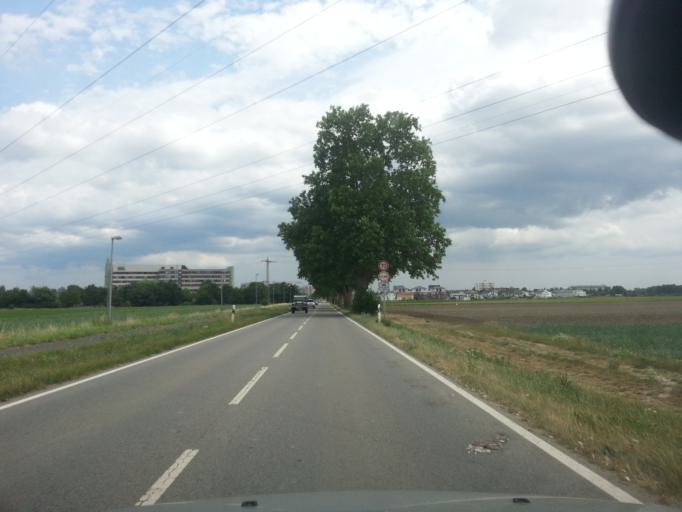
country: DE
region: Rheinland-Pfalz
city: Hessheim
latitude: 49.5423
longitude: 8.3245
